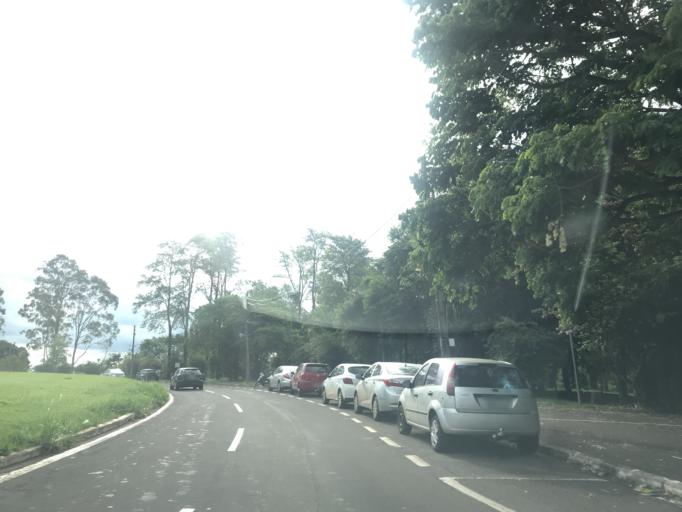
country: BR
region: Parana
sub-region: Maringa
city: Maringa
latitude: -23.4279
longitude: -51.9598
